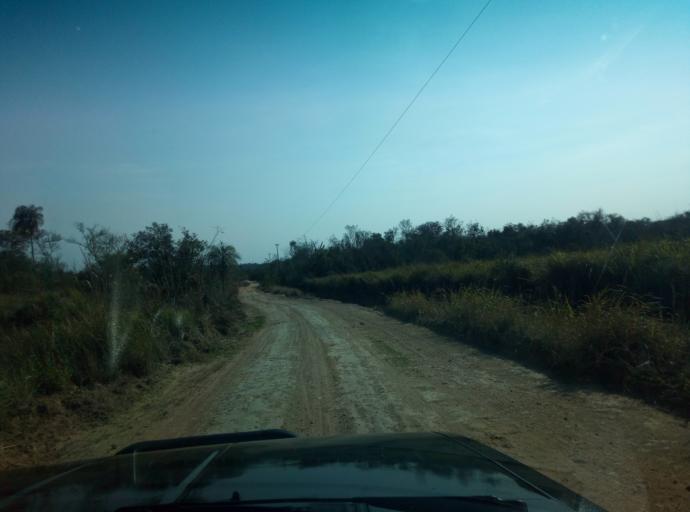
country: PY
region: Caaguazu
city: Doctor Cecilio Baez
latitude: -25.1901
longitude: -56.1917
